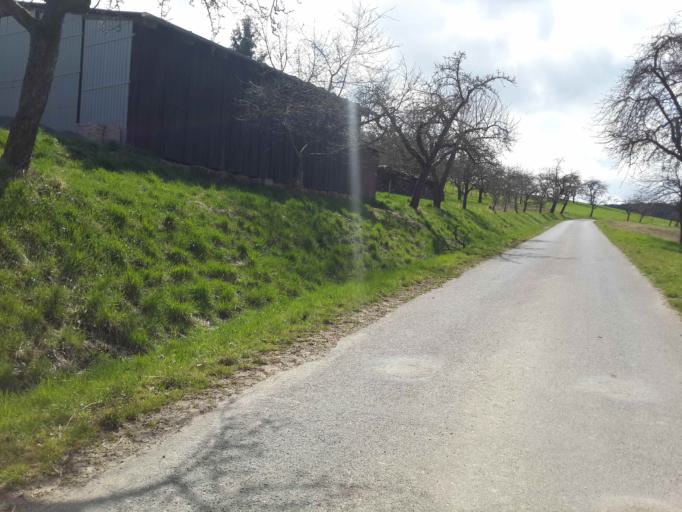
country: DE
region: Baden-Wuerttemberg
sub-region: Regierungsbezirk Stuttgart
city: Bad Mergentheim
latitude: 49.4423
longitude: 9.7498
